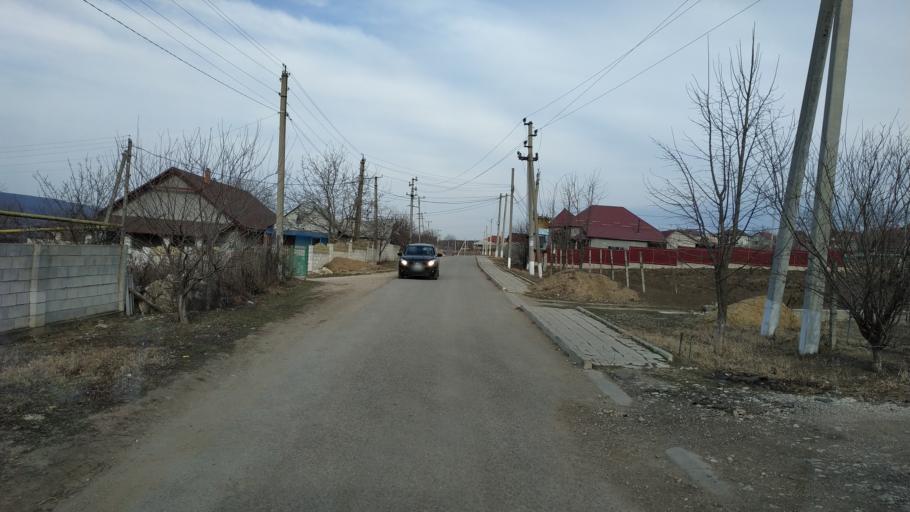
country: MD
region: Chisinau
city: Vatra
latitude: 46.9878
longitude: 28.6665
